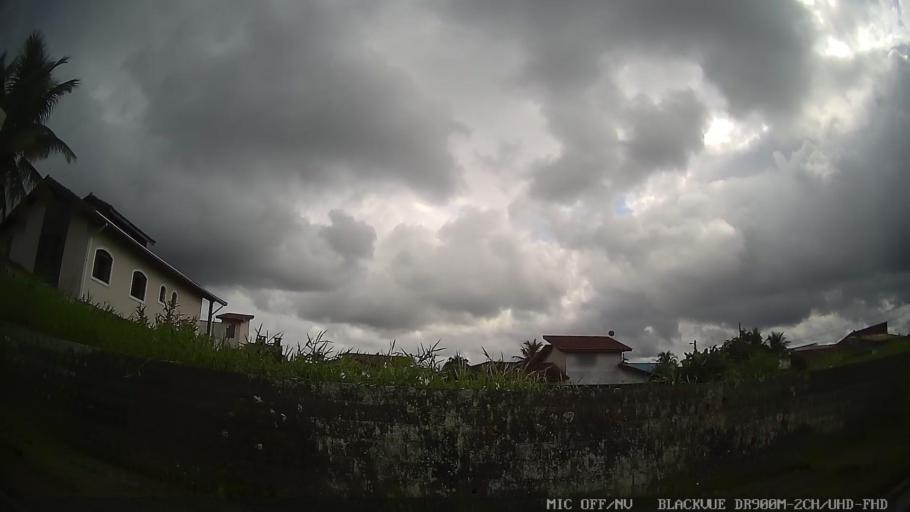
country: BR
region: Sao Paulo
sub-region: Itanhaem
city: Itanhaem
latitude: -24.2017
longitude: -46.8403
